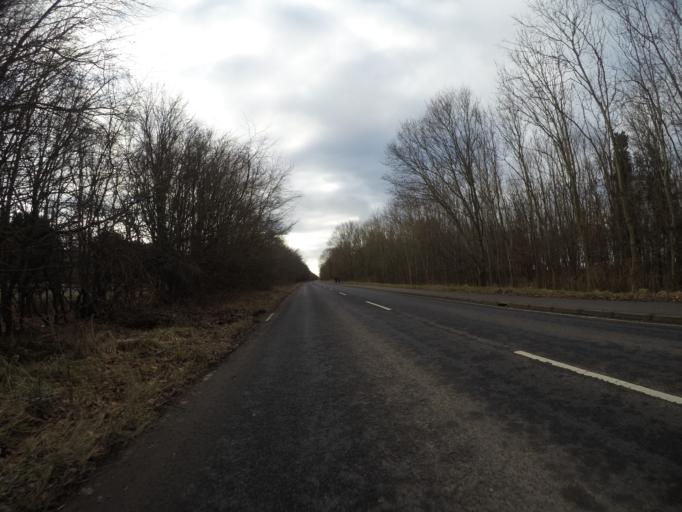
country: GB
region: Scotland
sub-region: North Ayrshire
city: Dreghorn
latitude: 55.5831
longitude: -4.6456
